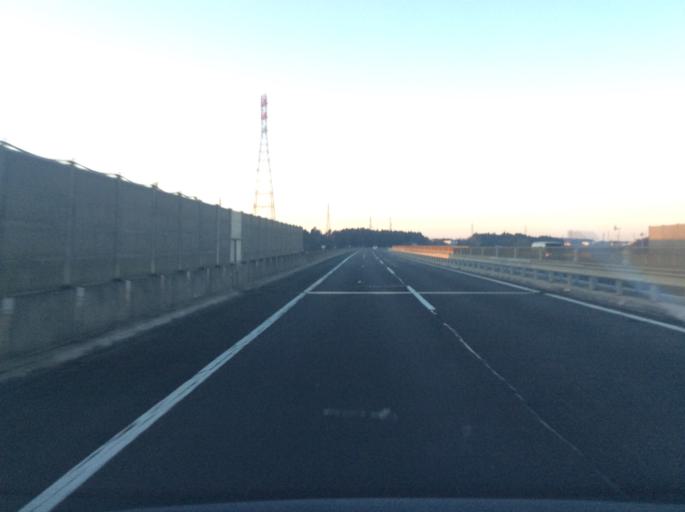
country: JP
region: Ibaraki
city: Funaishikawa
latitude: 36.4961
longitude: 140.5647
